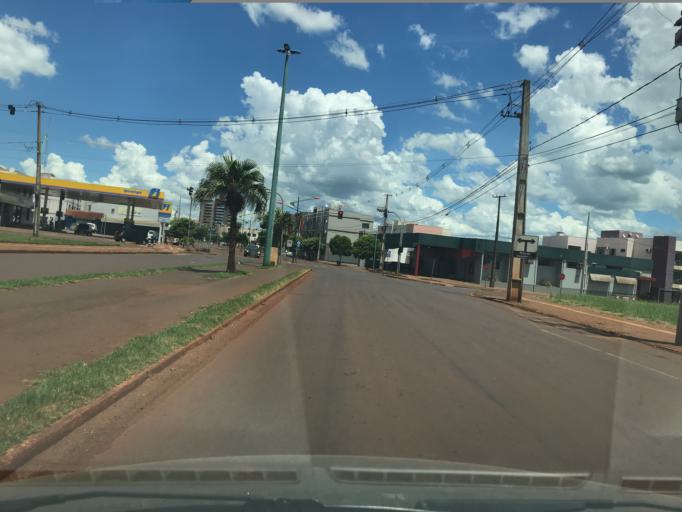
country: BR
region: Parana
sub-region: Palotina
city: Palotina
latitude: -24.2775
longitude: -53.8417
